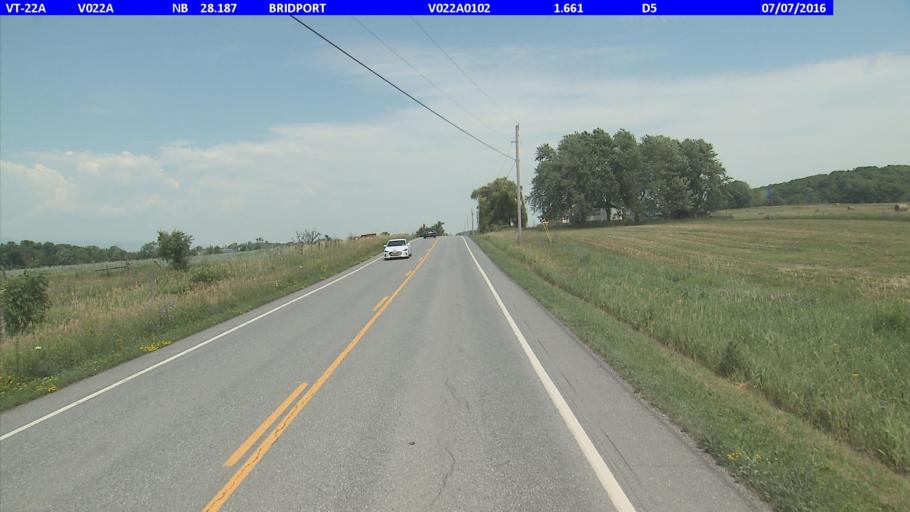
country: US
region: Vermont
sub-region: Addison County
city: Middlebury (village)
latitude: 43.9642
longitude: -73.3092
